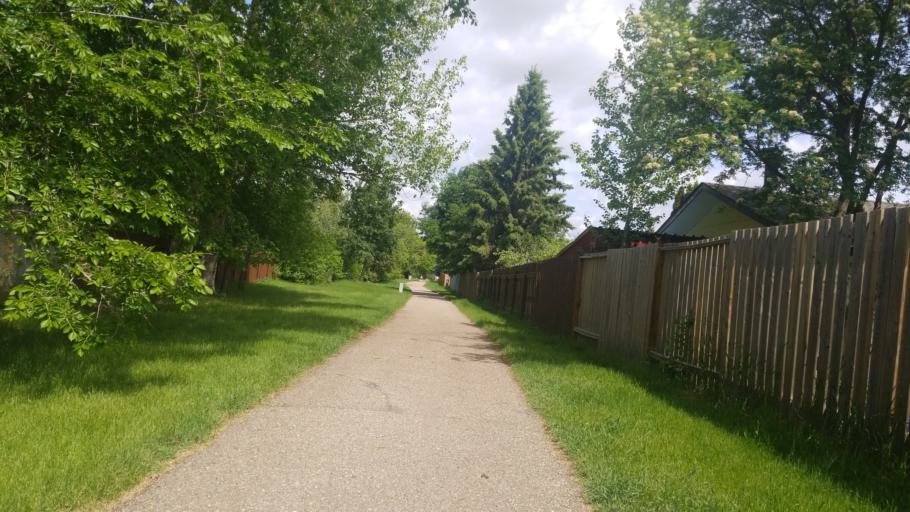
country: CA
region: Saskatchewan
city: Lloydminster
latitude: 53.2652
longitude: -110.0176
